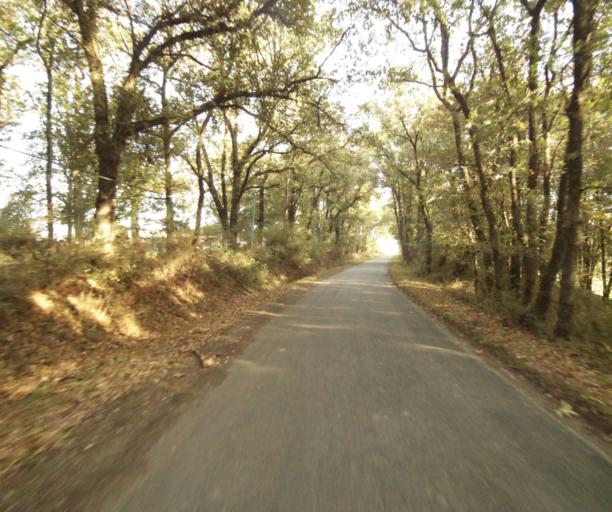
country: FR
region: Midi-Pyrenees
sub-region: Departement du Tarn-et-Garonne
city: Nohic
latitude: 43.9145
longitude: 1.4798
